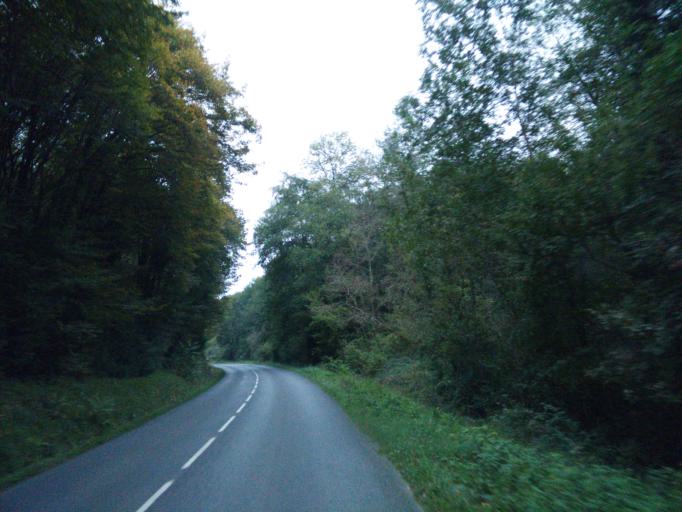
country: FR
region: Aquitaine
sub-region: Departement de la Dordogne
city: Carsac-Aillac
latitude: 44.8538
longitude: 1.2632
